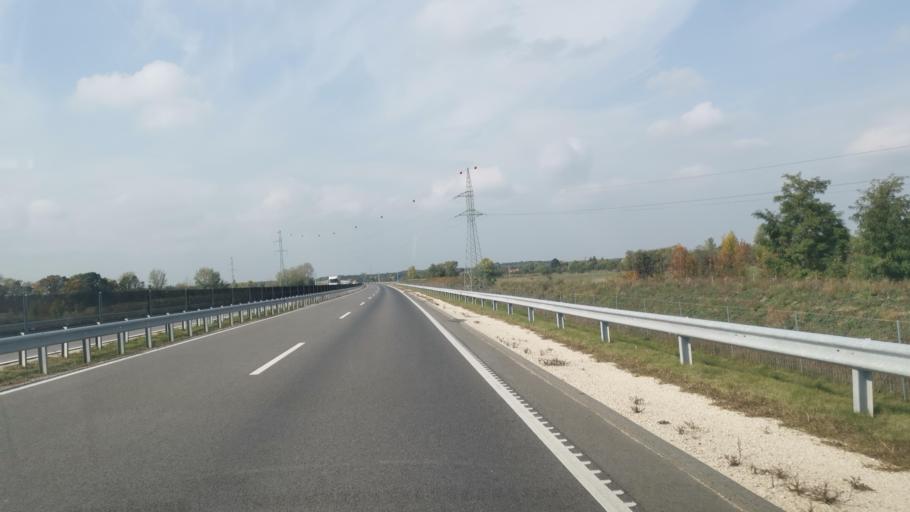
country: HU
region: Gyor-Moson-Sopron
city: Kapuvar
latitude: 47.5775
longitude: 16.9942
